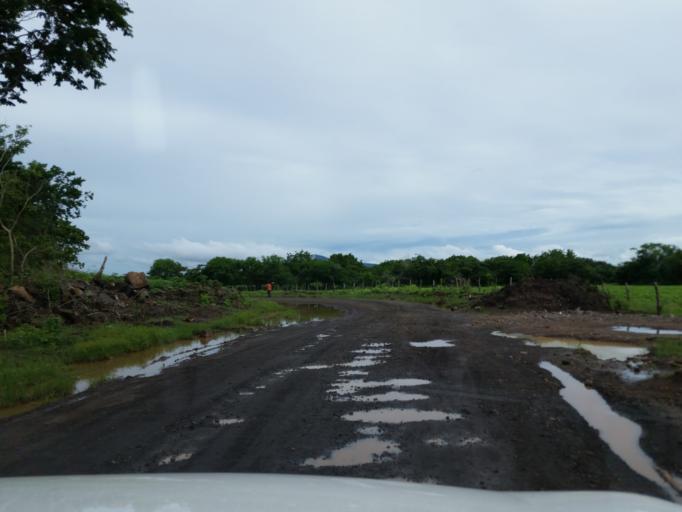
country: NI
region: Leon
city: Larreynaga
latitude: 12.5638
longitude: -86.6225
